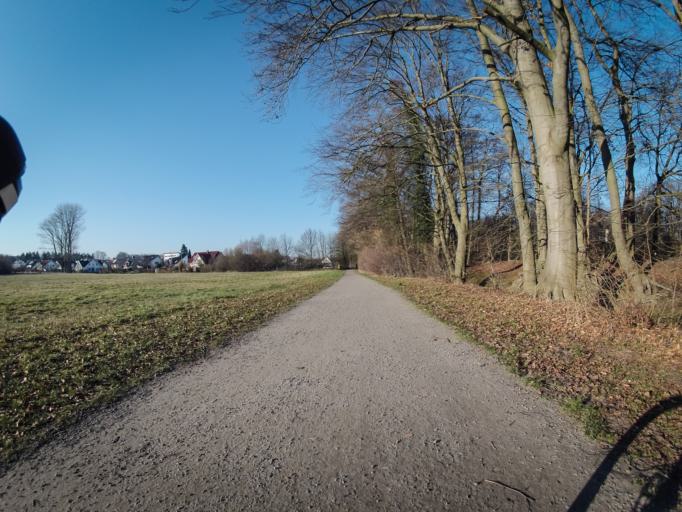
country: DE
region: Lower Saxony
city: Osnabrueck
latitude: 52.2915
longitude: 7.9875
